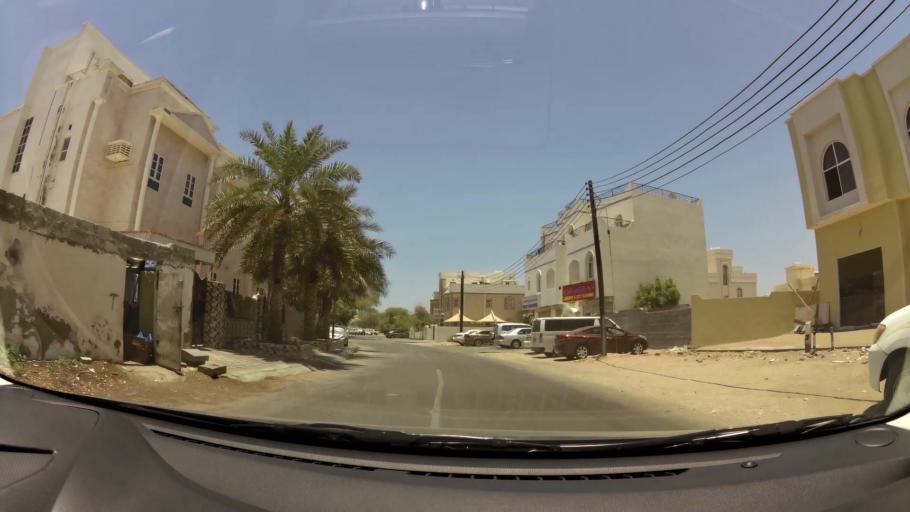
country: OM
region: Muhafazat Masqat
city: Bawshar
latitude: 23.5934
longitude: 58.3895
